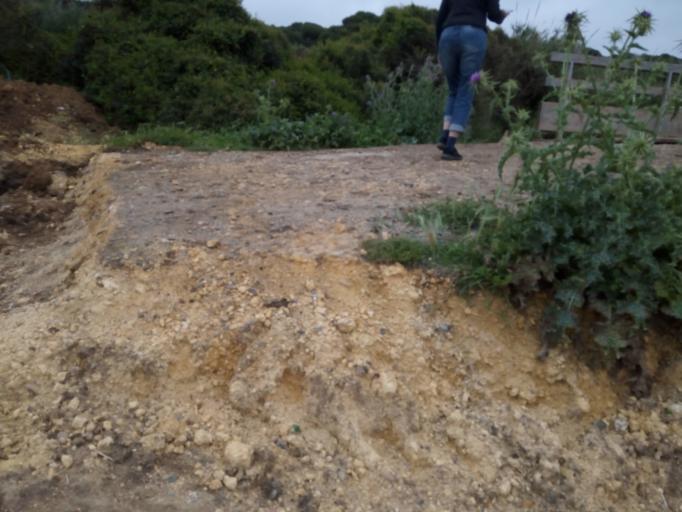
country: DZ
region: Tipaza
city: Tipasa
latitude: 36.5900
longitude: 2.4958
